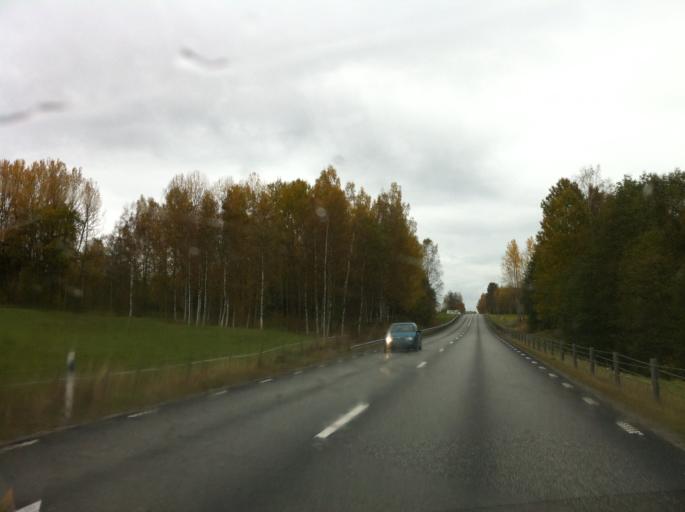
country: SE
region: OErebro
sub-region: Lindesbergs Kommun
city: Stora
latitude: 59.6791
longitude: 15.0993
